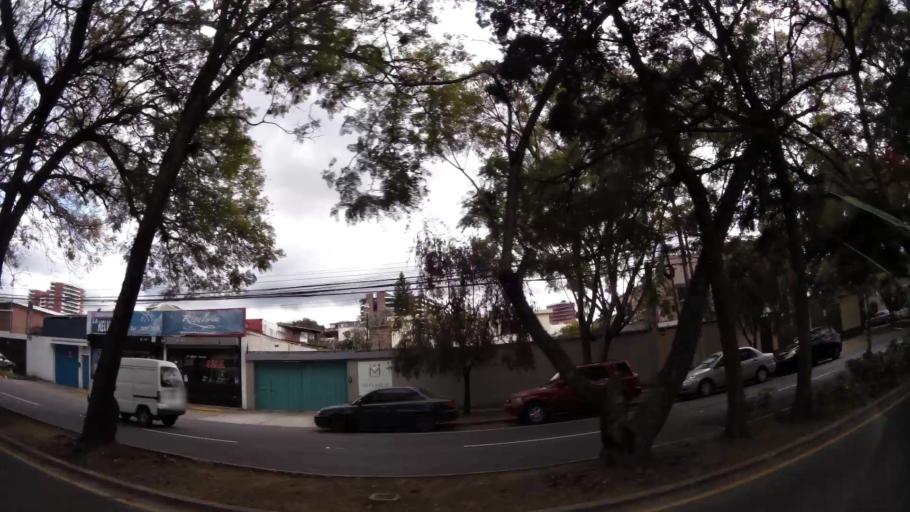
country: GT
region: Guatemala
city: Santa Catarina Pinula
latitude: 14.5849
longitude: -90.5228
